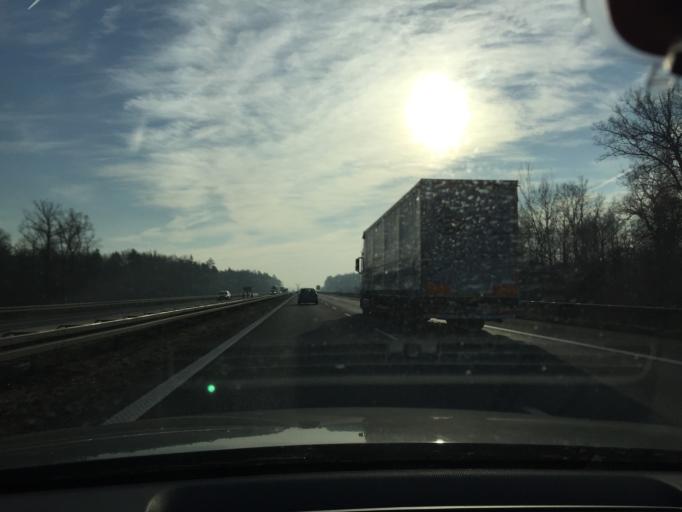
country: PL
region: Silesian Voivodeship
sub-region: Powiat gliwicki
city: Sosnicowice
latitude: 50.3247
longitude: 18.5475
